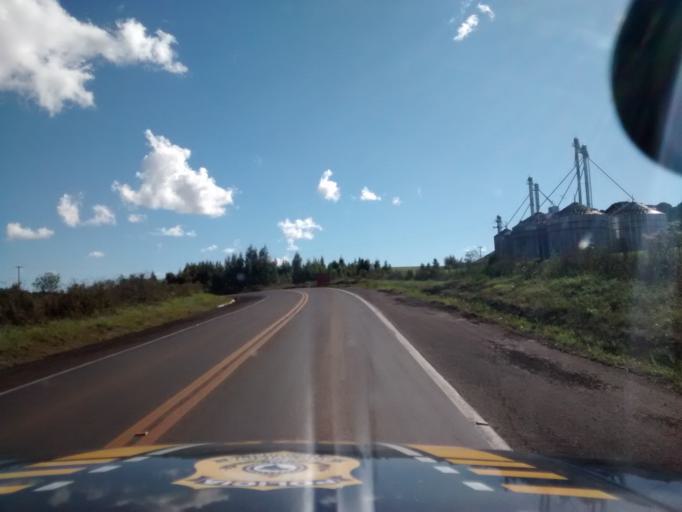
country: BR
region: Rio Grande do Sul
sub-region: Lagoa Vermelha
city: Lagoa Vermelha
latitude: -28.2934
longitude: -51.4336
